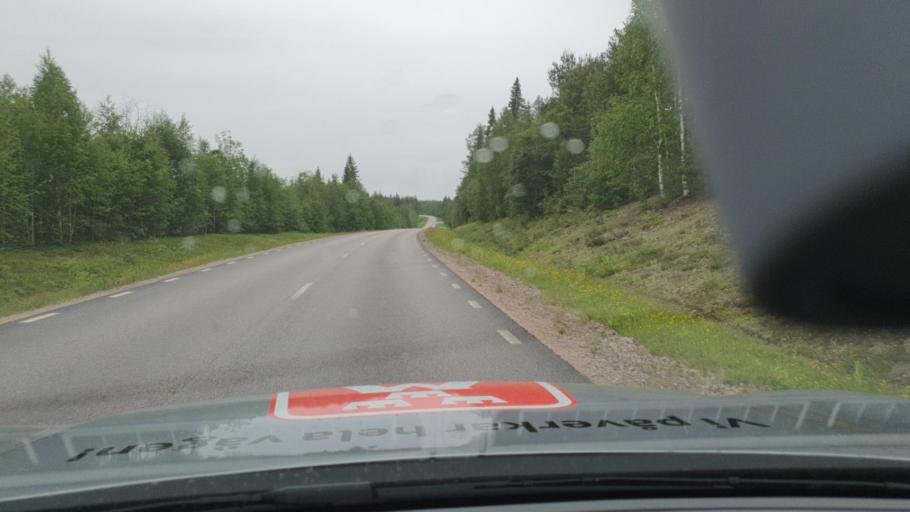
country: SE
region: Norrbotten
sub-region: Overtornea Kommun
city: OEvertornea
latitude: 66.4033
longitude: 23.4858
